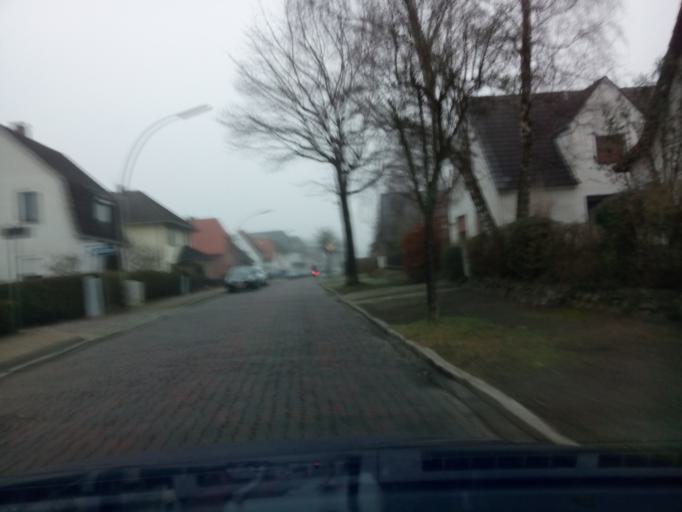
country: DE
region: Lower Saxony
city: Osterholz-Scharmbeck
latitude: 53.2221
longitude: 8.7905
